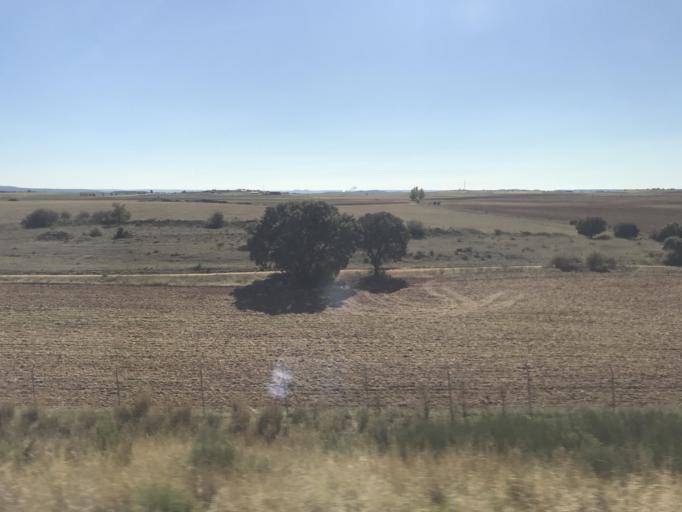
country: ES
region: Castille-La Mancha
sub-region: Provincia de Guadalajara
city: Alaminos
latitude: 40.8807
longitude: -2.7453
